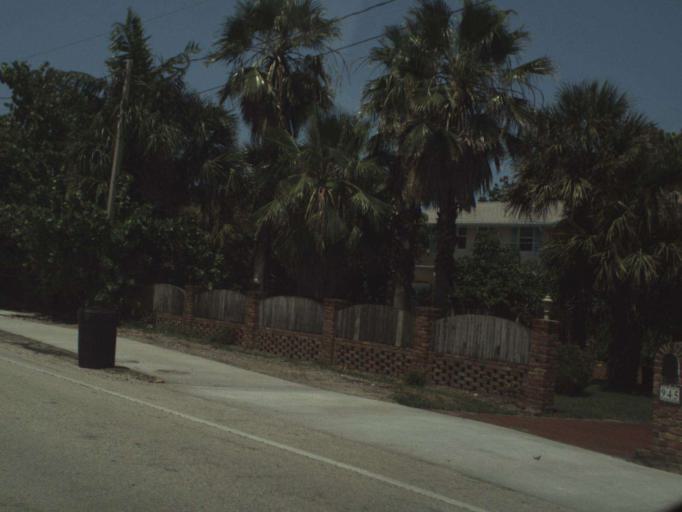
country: US
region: Florida
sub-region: Brevard County
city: Cocoa Beach
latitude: 28.3014
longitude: -80.6086
